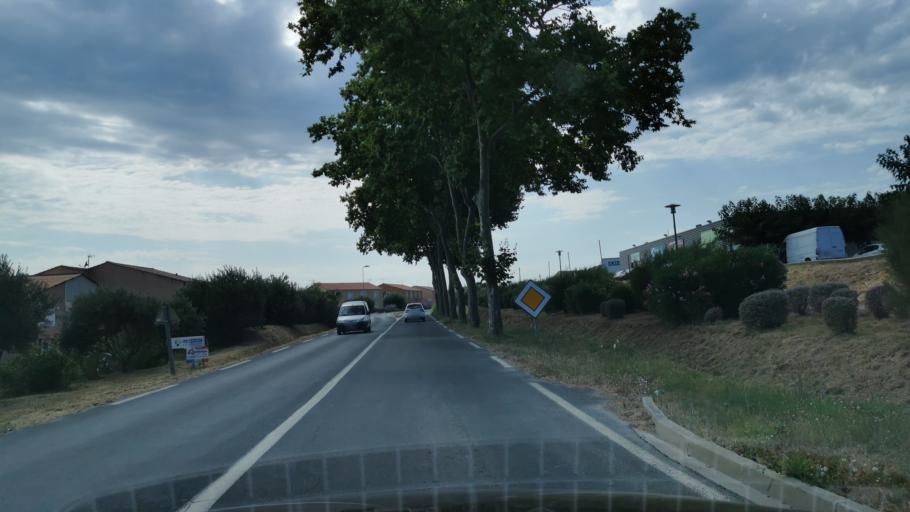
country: FR
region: Languedoc-Roussillon
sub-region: Departement de l'Herault
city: Puisserguier
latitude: 43.3666
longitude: 3.0511
